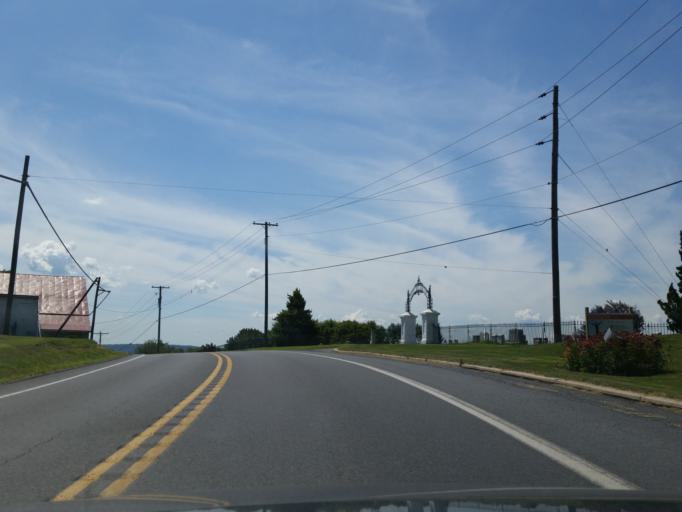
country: US
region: Pennsylvania
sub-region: Lebanon County
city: Palmyra
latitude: 40.3229
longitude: -76.6063
